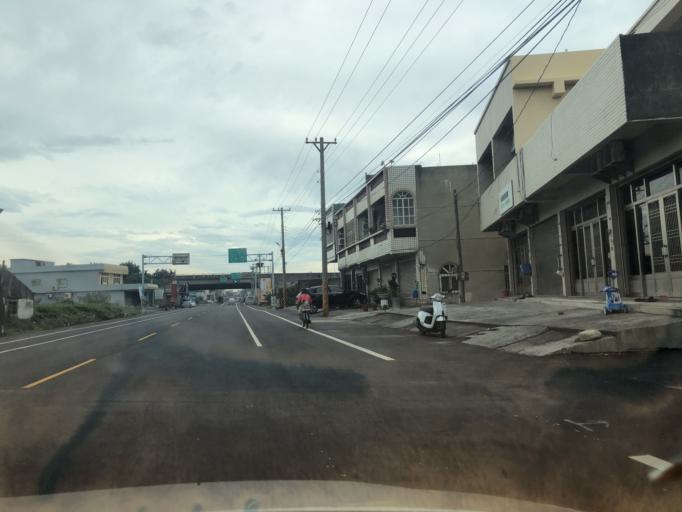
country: TW
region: Taiwan
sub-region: Chiayi
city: Taibao
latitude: 23.7110
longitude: 120.2010
